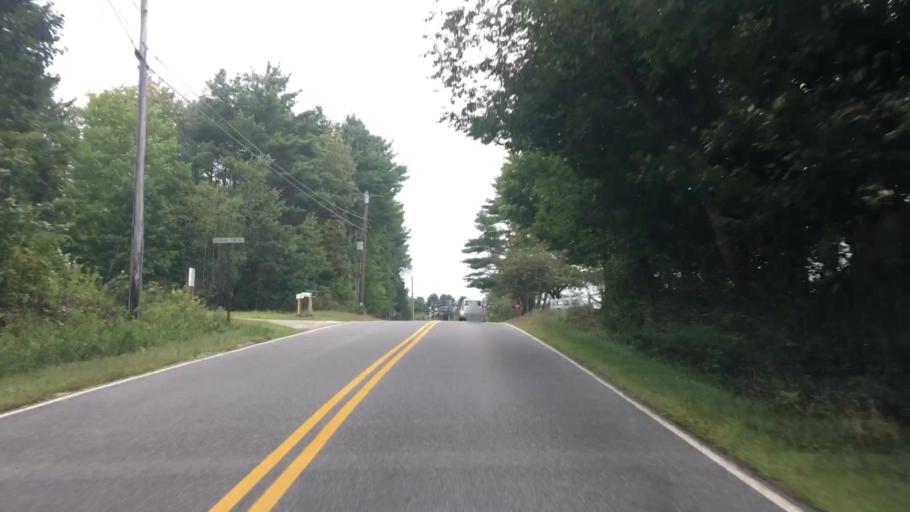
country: US
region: Maine
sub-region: Cumberland County
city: Yarmouth
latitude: 43.8622
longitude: -70.2218
